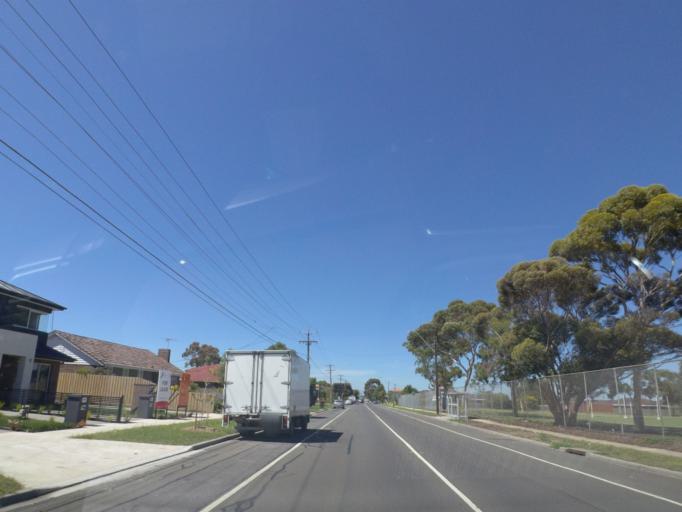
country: AU
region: Victoria
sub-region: Hume
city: Tullamarine
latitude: -37.7030
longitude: 144.8796
